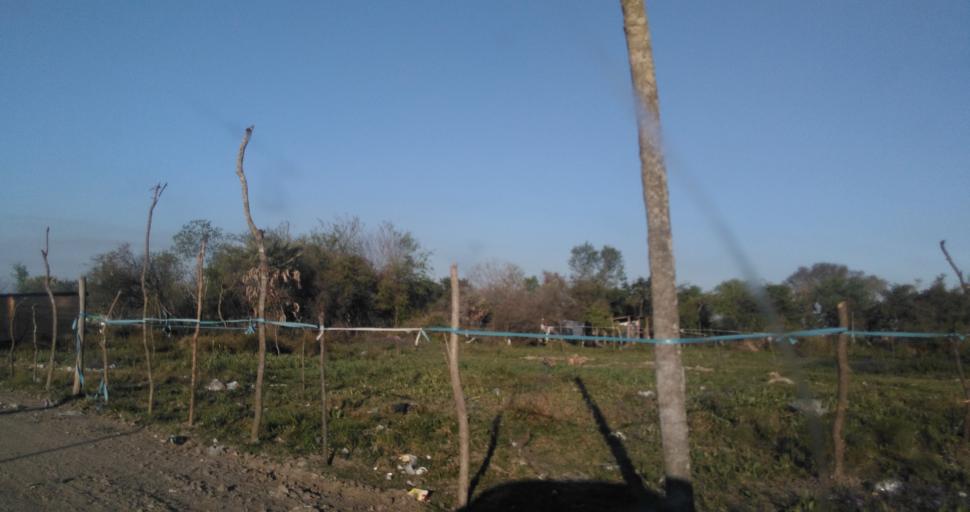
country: AR
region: Chaco
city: Fontana
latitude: -27.4672
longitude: -59.0347
